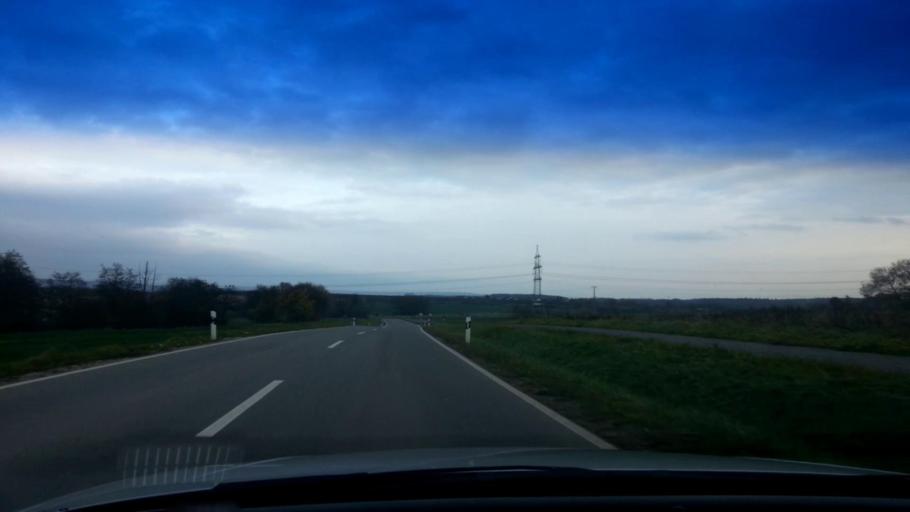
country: DE
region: Bavaria
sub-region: Upper Franconia
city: Memmelsdorf
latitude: 49.9569
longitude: 10.9626
